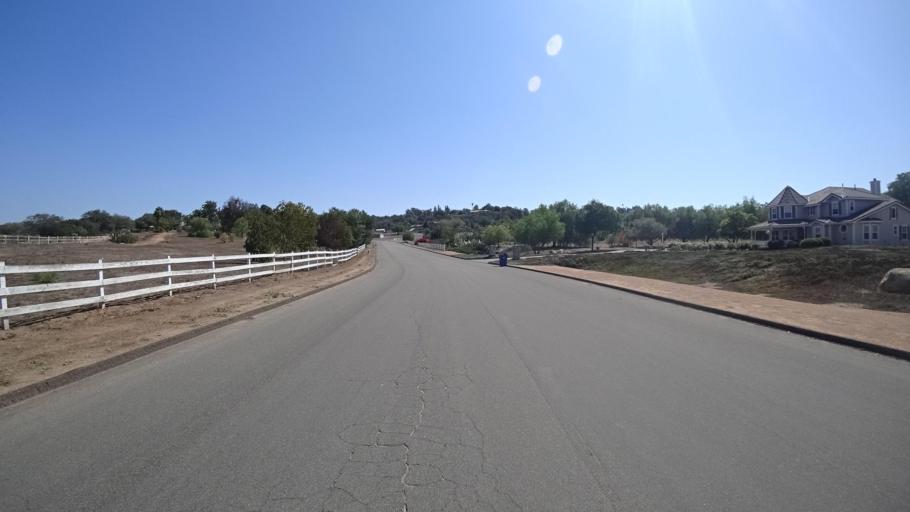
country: US
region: California
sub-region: San Diego County
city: Crest
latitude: 32.8267
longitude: -116.8553
